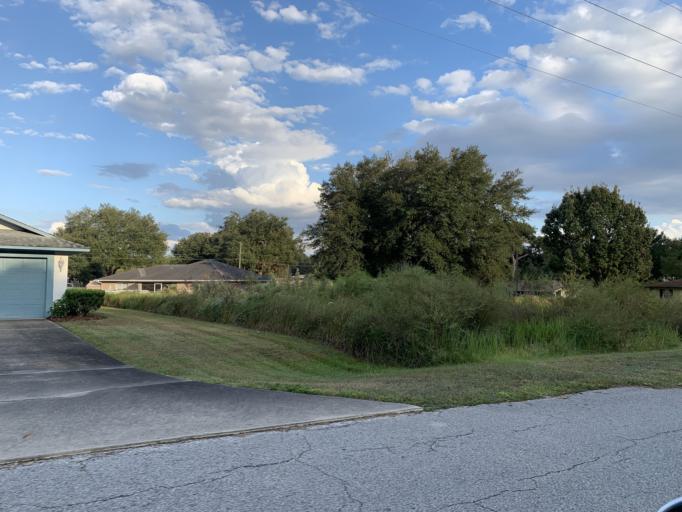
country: US
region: Florida
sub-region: Marion County
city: Silver Springs Shores
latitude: 29.1615
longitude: -82.0444
